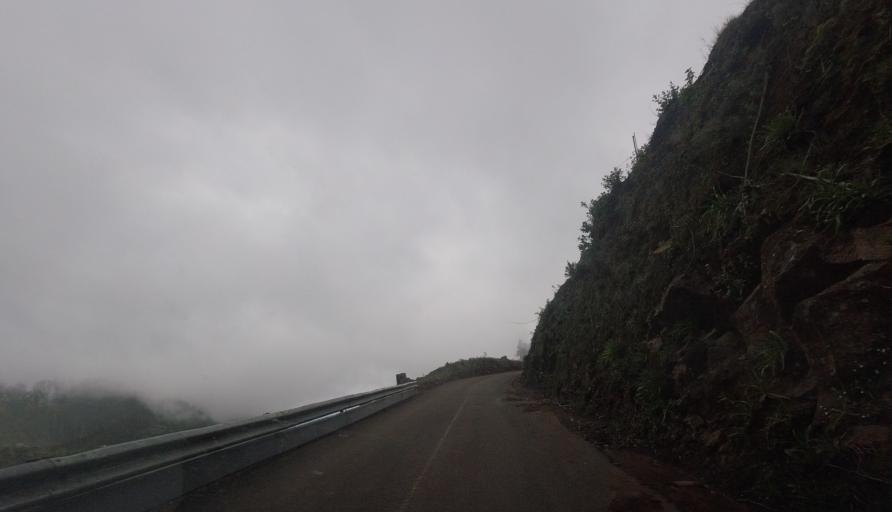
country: PT
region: Madeira
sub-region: Funchal
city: Nossa Senhora do Monte
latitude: 32.6917
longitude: -16.8968
